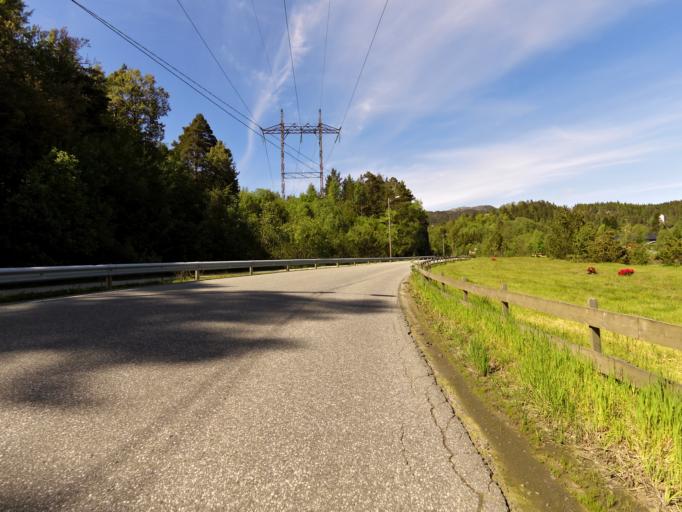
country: NO
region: Hordaland
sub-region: Stord
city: Sagvag
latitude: 59.7858
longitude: 5.4145
